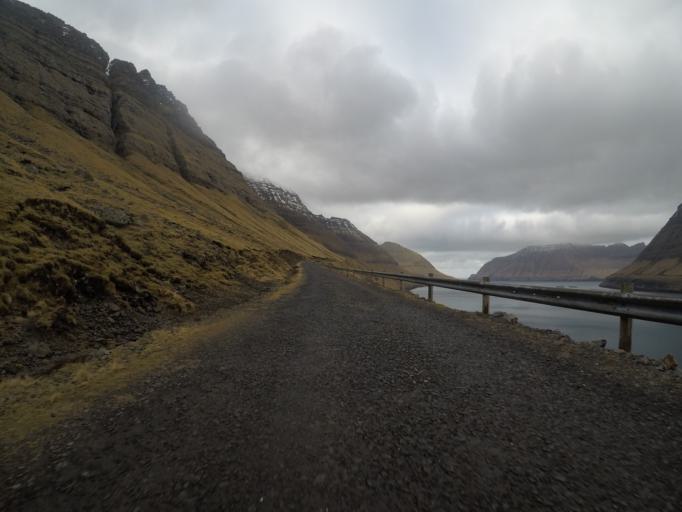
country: FO
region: Nordoyar
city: Klaksvik
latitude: 62.3246
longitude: -6.5633
